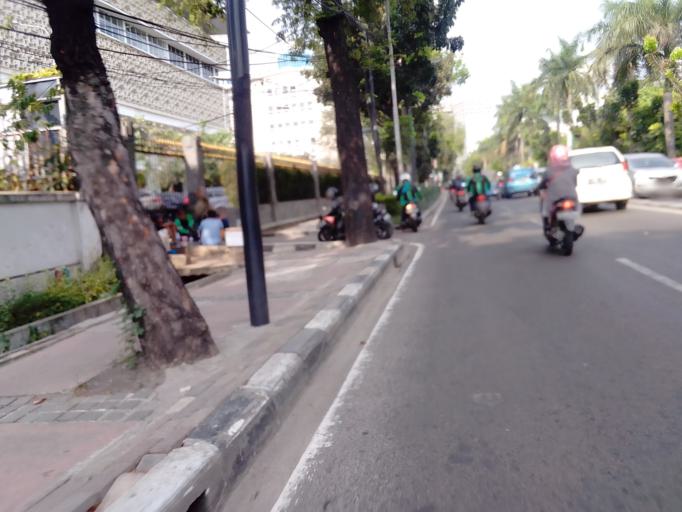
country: ID
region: Jakarta Raya
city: Jakarta
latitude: -6.1821
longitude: 106.8174
